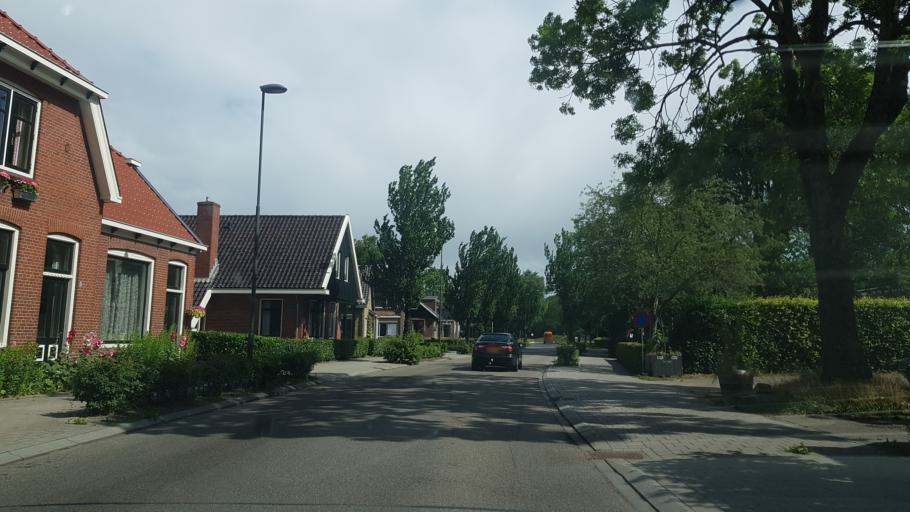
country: NL
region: Friesland
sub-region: Gemeente Tytsjerksteradiel
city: Oentsjerk
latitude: 53.2542
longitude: 5.8956
